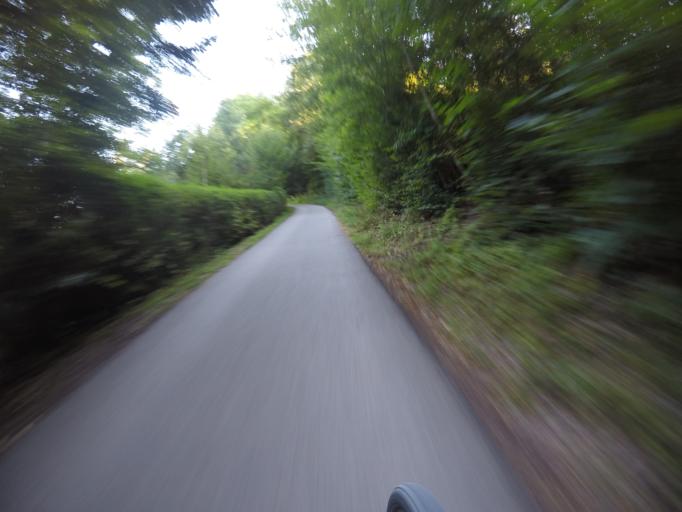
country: DE
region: Baden-Wuerttemberg
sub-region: Regierungsbezirk Stuttgart
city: Waldenbuch
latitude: 48.6393
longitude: 9.1181
